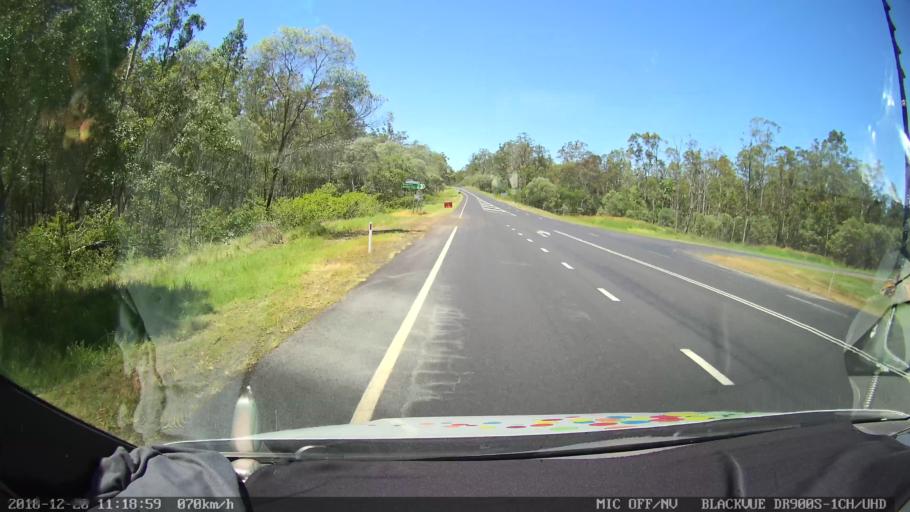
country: AU
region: New South Wales
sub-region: Richmond Valley
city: Casino
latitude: -29.0576
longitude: 153.0054
